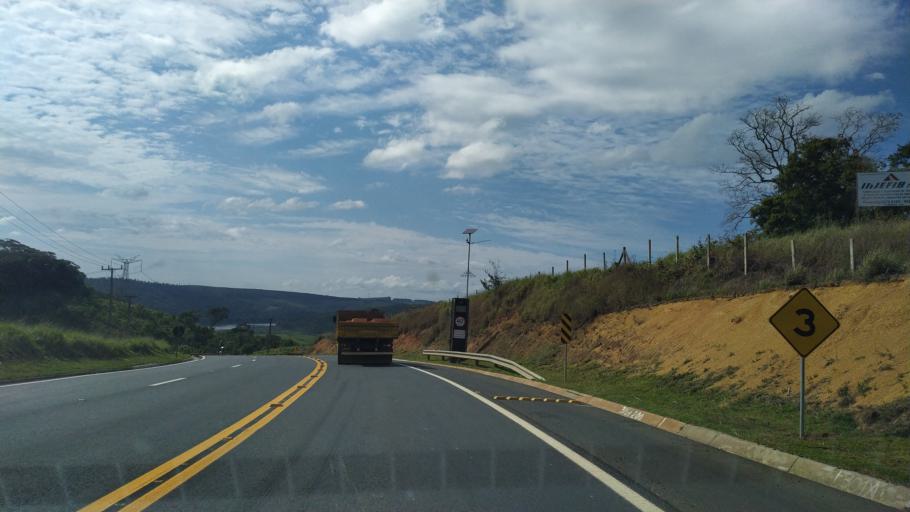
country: BR
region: Parana
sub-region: Telemaco Borba
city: Telemaco Borba
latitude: -24.2859
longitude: -50.7076
